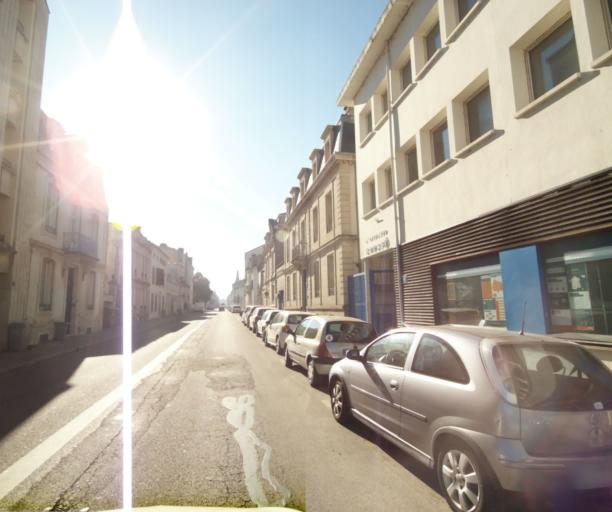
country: FR
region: Lorraine
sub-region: Departement de Meurthe-et-Moselle
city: Maxeville
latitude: 48.7044
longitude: 6.1696
